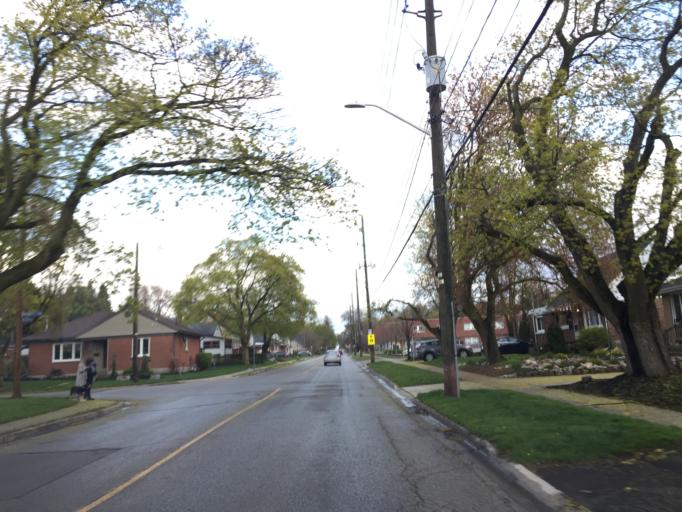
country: CA
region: Ontario
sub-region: Wellington County
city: Guelph
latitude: 43.5561
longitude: -80.2482
